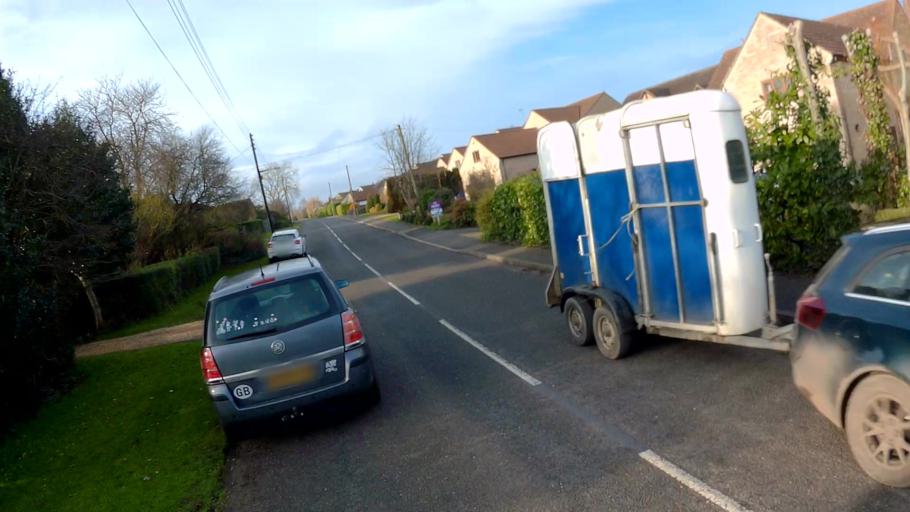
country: GB
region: England
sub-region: Lincolnshire
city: Bourne
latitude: 52.7364
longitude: -0.3890
